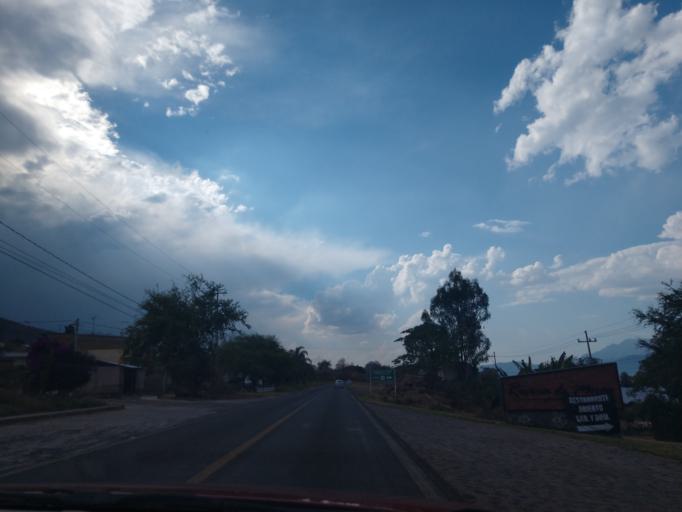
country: MX
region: Jalisco
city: San Juan Cosala
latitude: 20.2027
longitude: -103.3135
